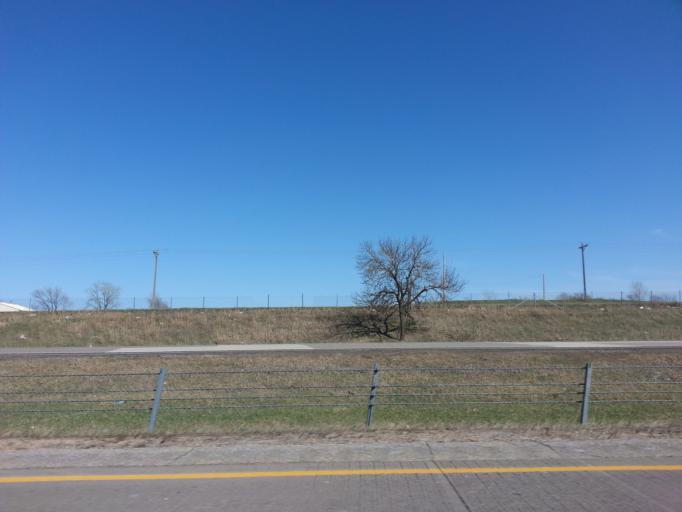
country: US
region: Minnesota
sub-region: Dakota County
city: Lakeville
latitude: 44.6615
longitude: -93.2941
